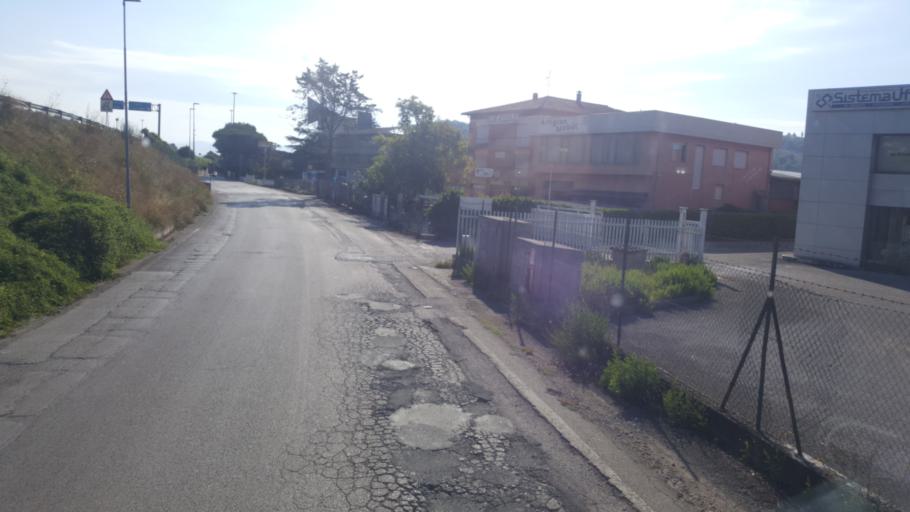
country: IT
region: Umbria
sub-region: Provincia di Perugia
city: Via Lippia
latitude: 43.0856
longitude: 12.4410
